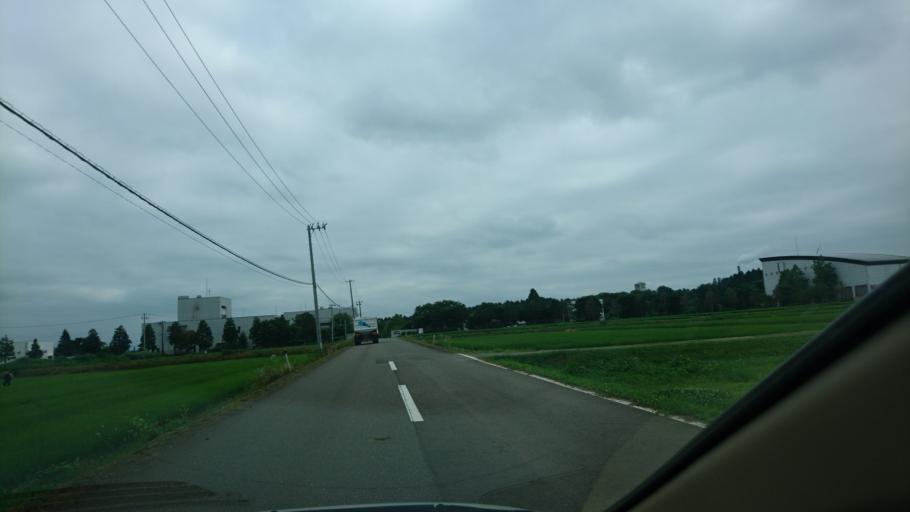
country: JP
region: Iwate
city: Kitakami
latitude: 39.2370
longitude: 141.0999
